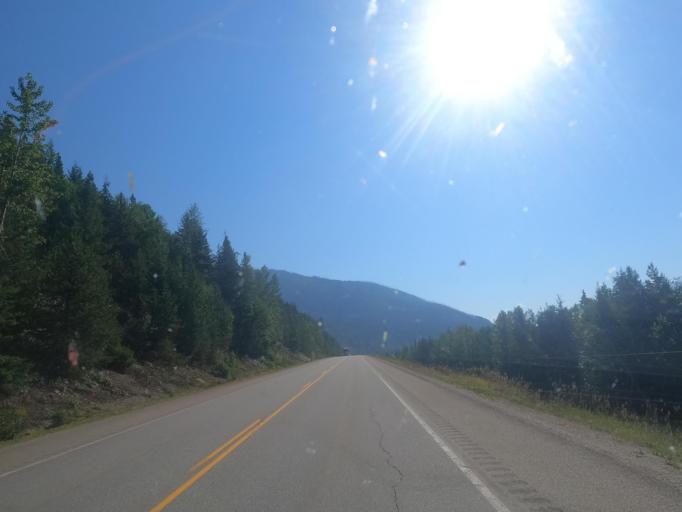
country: CA
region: Alberta
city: Jasper Park Lodge
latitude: 52.9544
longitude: -118.8826
